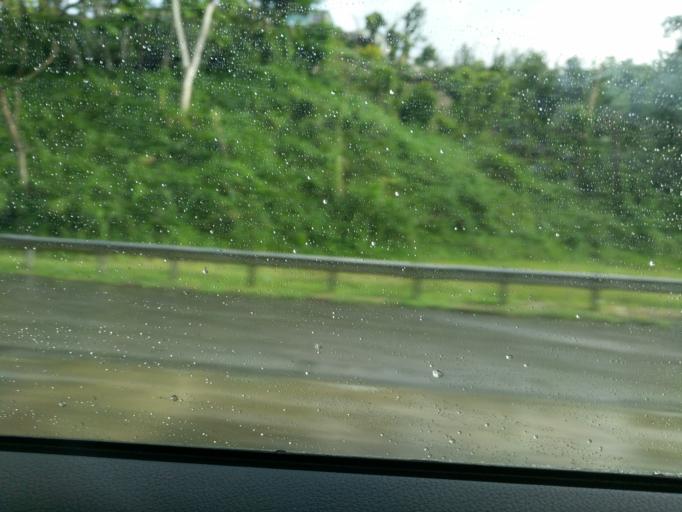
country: PR
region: Cidra
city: Bayamon
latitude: 18.1654
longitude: -66.0823
